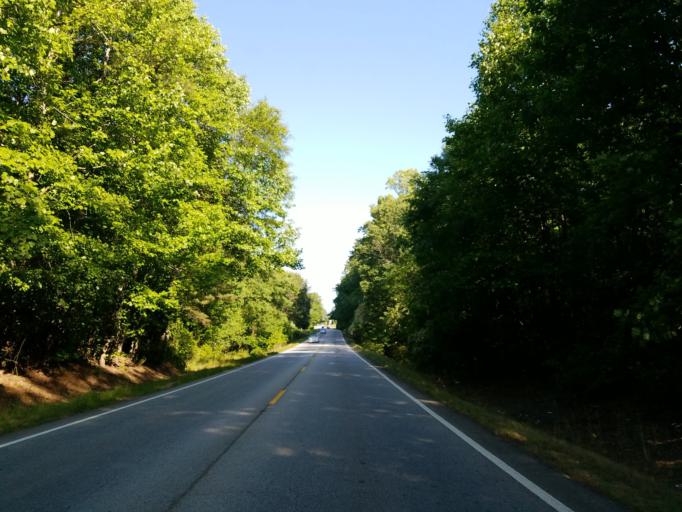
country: US
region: Georgia
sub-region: Carroll County
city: Villa Rica
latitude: 33.7580
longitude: -84.9408
